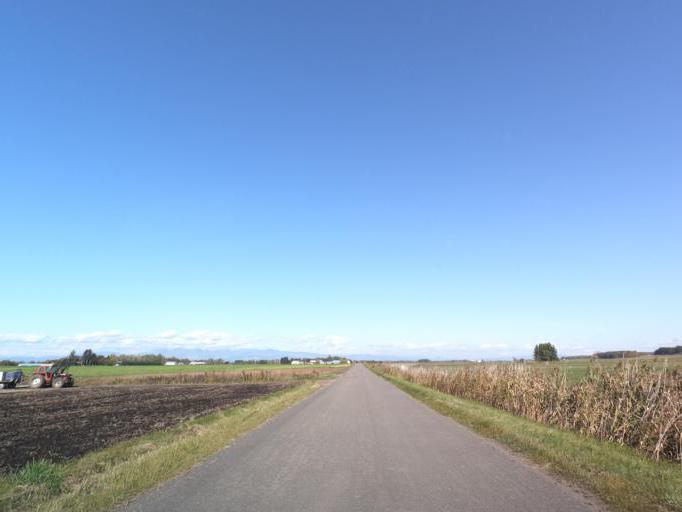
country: JP
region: Hokkaido
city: Otofuke
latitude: 43.0190
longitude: 143.2679
